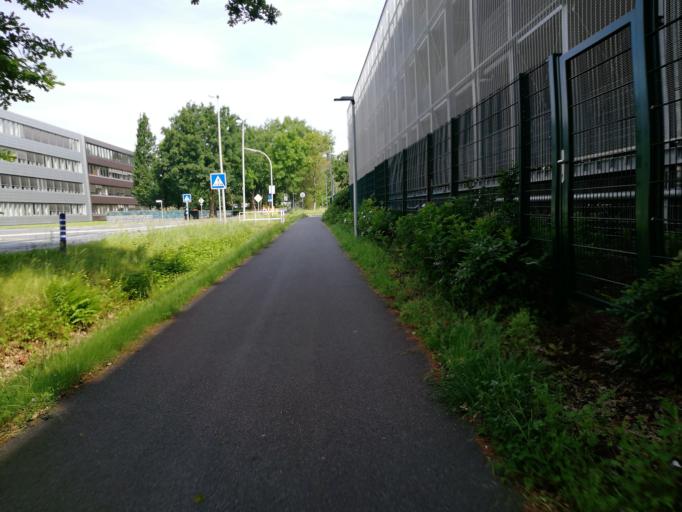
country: DE
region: North Rhine-Westphalia
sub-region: Regierungsbezirk Detmold
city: Verl
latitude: 51.8913
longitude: 8.4554
